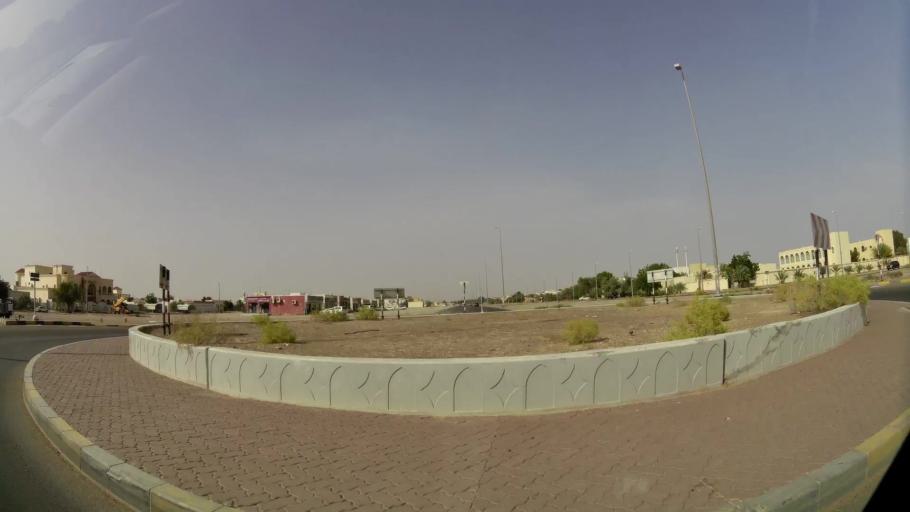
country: AE
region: Abu Dhabi
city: Al Ain
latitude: 24.2080
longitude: 55.5887
